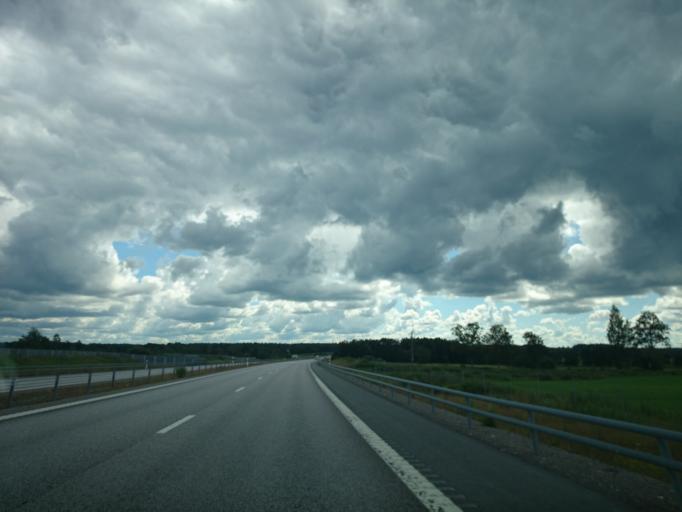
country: SE
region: Uppsala
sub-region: Tierps Kommun
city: Tierp
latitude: 60.3283
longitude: 17.5064
